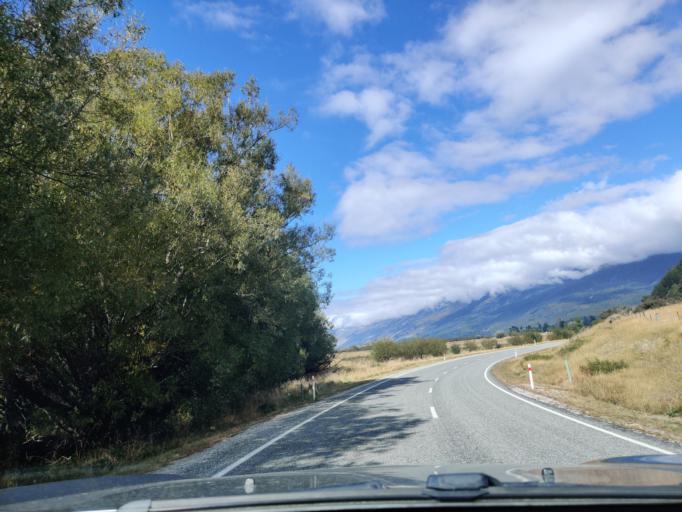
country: NZ
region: Otago
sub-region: Queenstown-Lakes District
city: Queenstown
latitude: -44.7901
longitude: 168.3871
